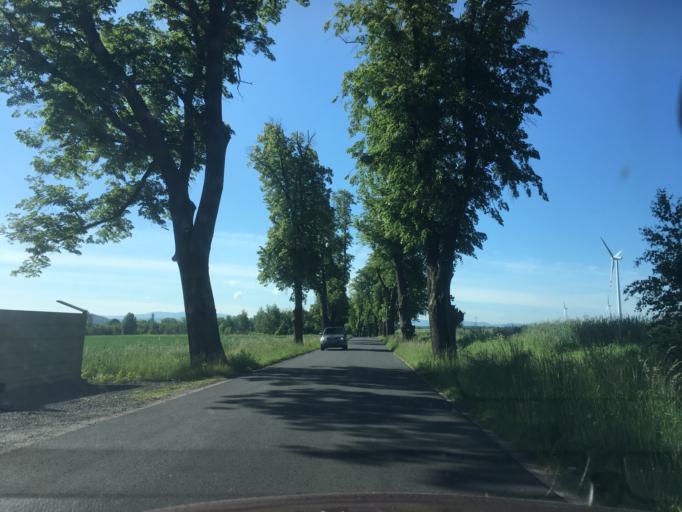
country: PL
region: Lower Silesian Voivodeship
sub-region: Powiat zgorzelecki
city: Sulikow
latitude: 51.1001
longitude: 15.0384
